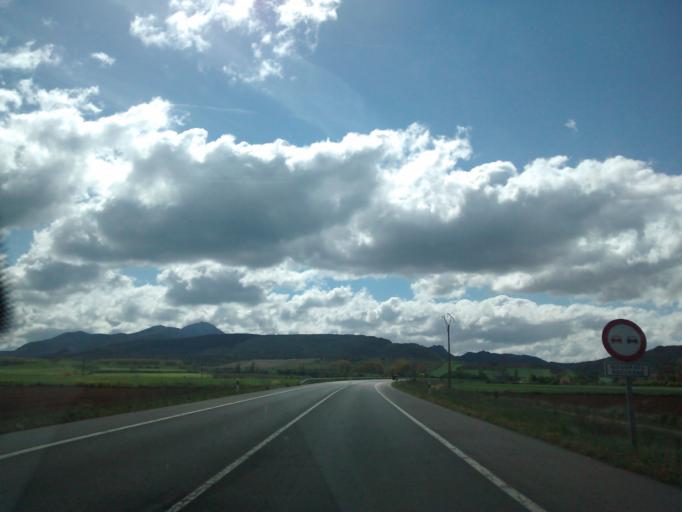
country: ES
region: Basque Country
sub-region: Provincia de Alava
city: Zambrana
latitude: 42.6547
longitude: -2.8783
